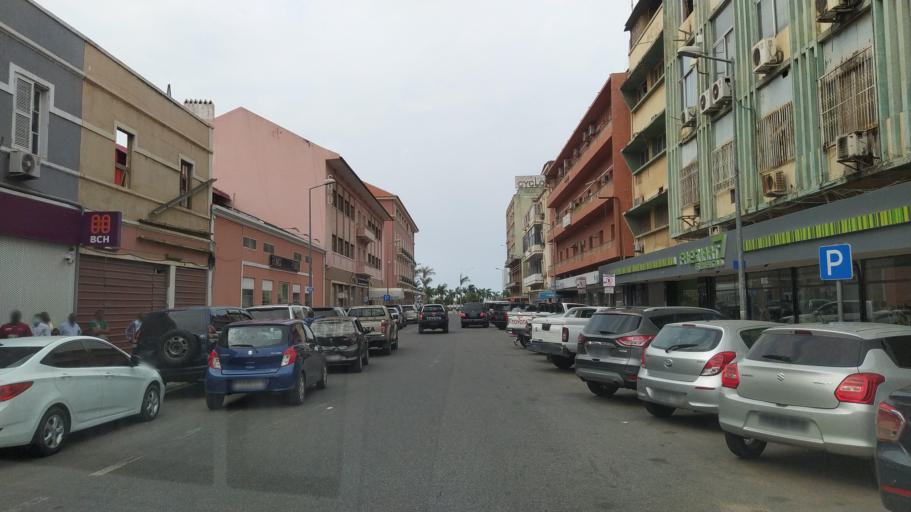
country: AO
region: Luanda
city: Luanda
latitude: -8.8116
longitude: 13.2351
